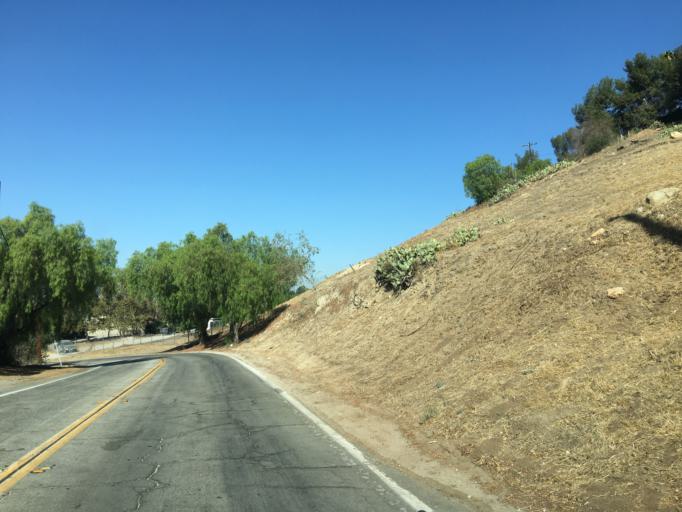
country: US
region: California
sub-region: Los Angeles County
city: San Fernando
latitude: 34.2836
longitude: -118.3759
